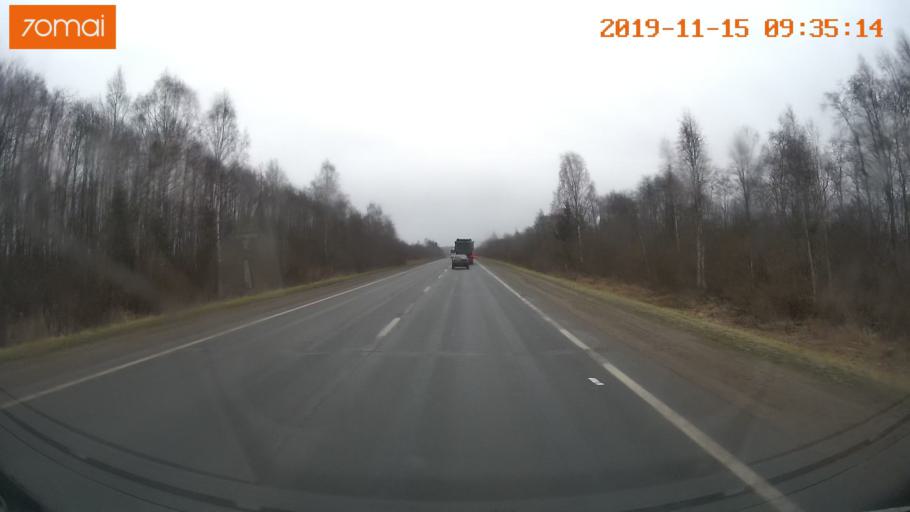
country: RU
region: Vologda
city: Sheksna
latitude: 59.2558
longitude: 38.3943
